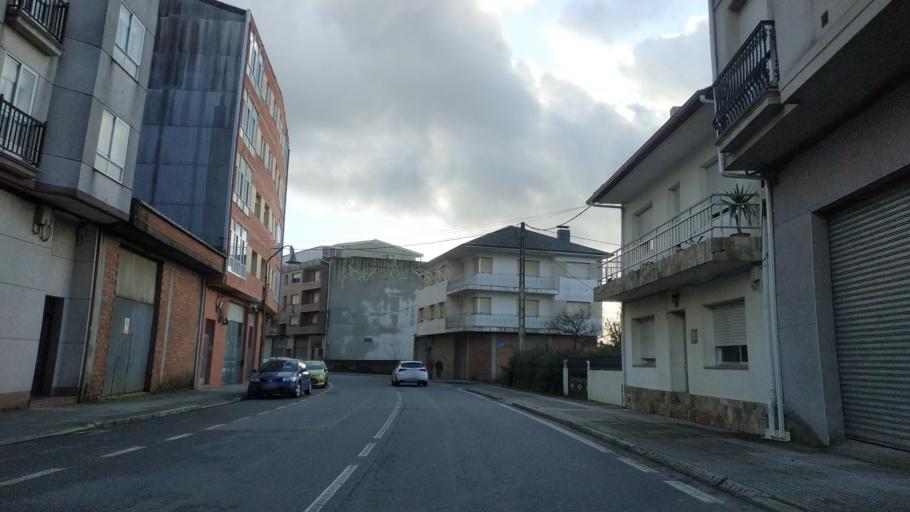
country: ES
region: Galicia
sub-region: Provincia da Coruna
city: Arzua
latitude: 42.9233
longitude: -8.1656
